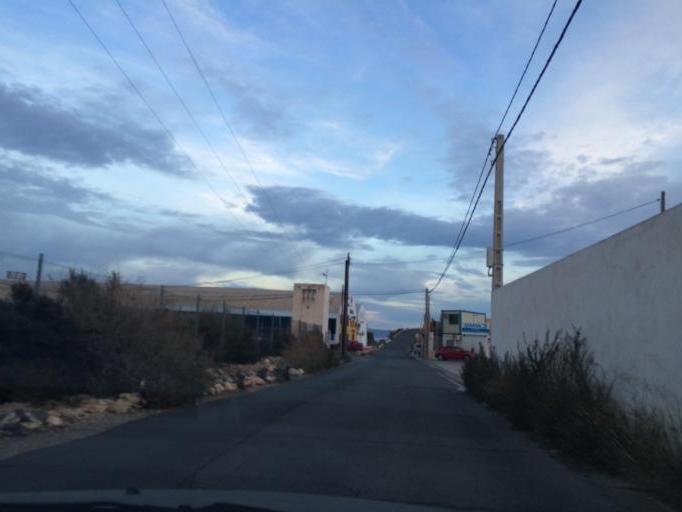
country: ES
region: Andalusia
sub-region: Provincia de Almeria
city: Viator
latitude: 36.8449
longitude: -2.4008
